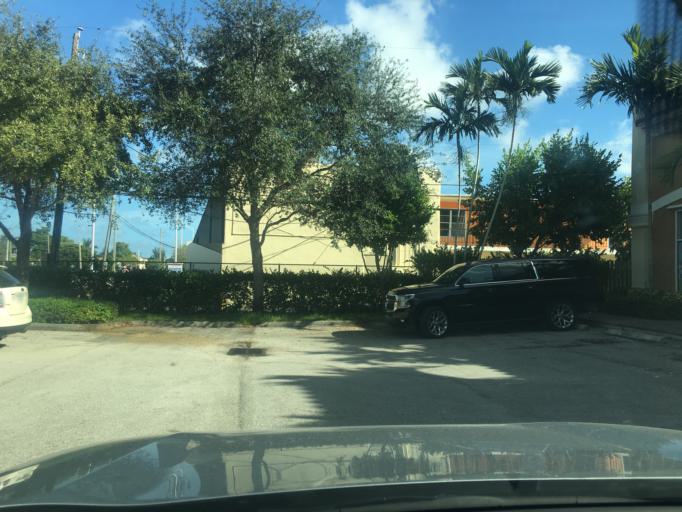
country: US
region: Florida
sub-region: Broward County
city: Dania Beach
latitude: 26.0621
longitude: -80.1826
